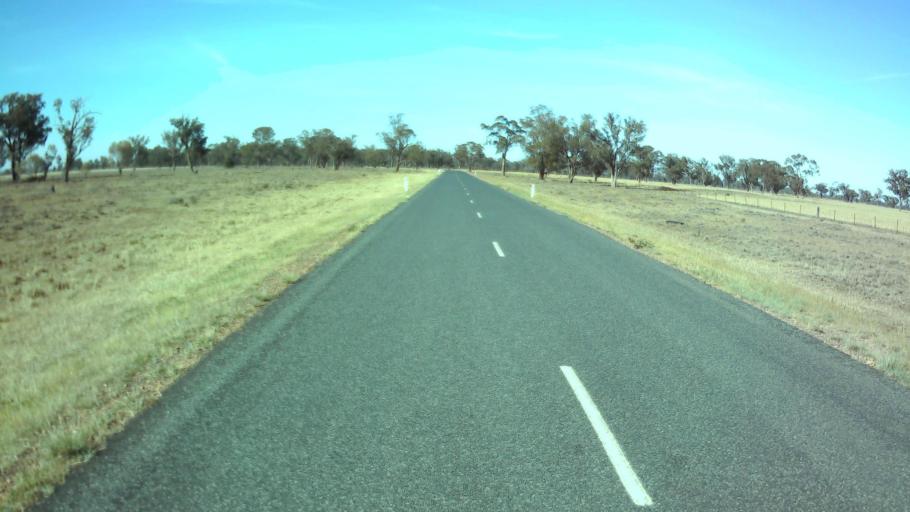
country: AU
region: New South Wales
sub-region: Weddin
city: Grenfell
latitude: -34.0562
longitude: 147.9139
